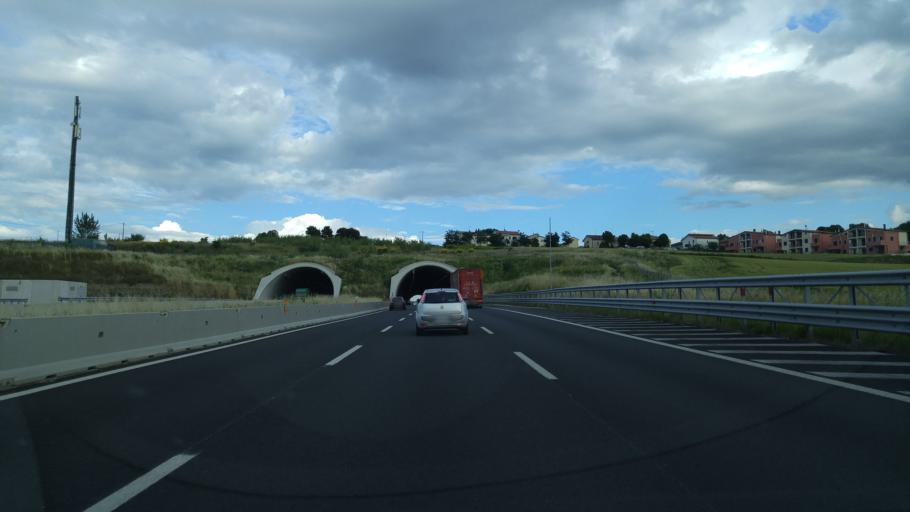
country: IT
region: Emilia-Romagna
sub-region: Provincia di Rimini
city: Riccione
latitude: 43.9803
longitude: 12.6534
